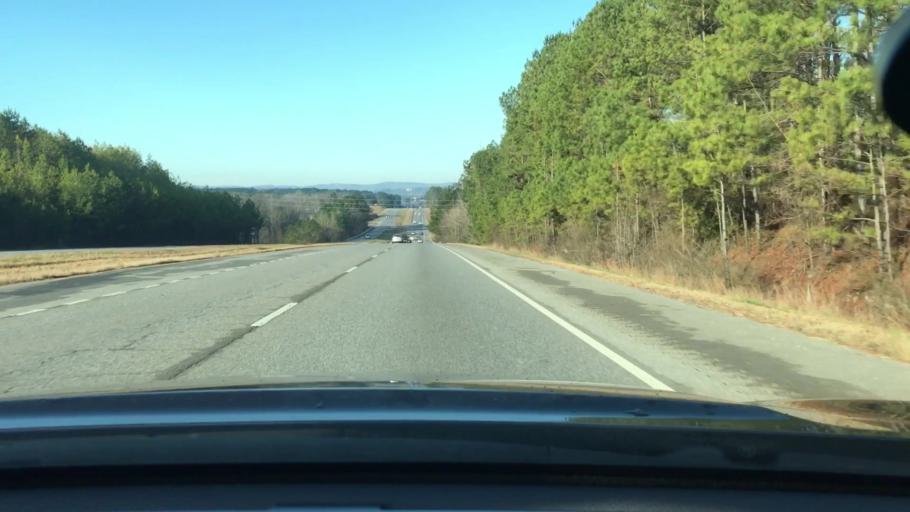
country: US
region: Alabama
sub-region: Shelby County
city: Chelsea
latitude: 33.3503
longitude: -86.5878
